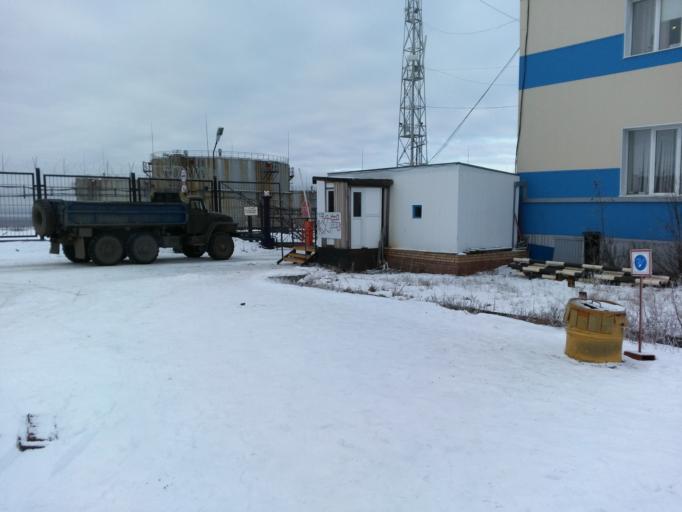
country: RU
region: Krasnoyarskiy
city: Dudinka
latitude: 69.4224
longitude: 86.1596
